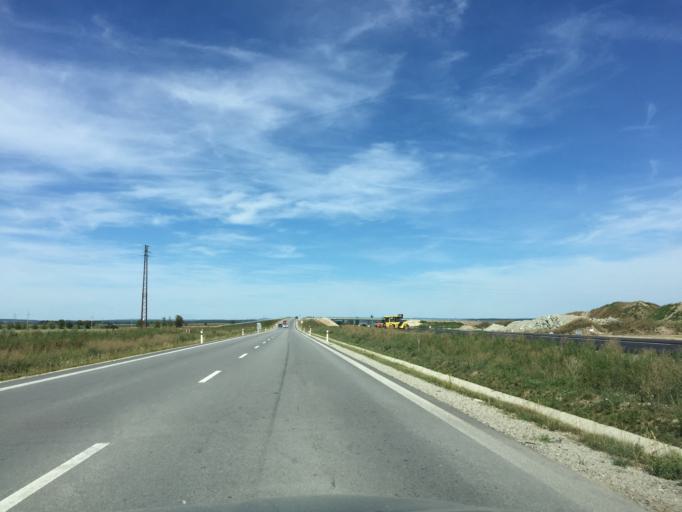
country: CZ
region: Jihocesky
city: Dolni Bukovsko
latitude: 49.1507
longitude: 14.6288
